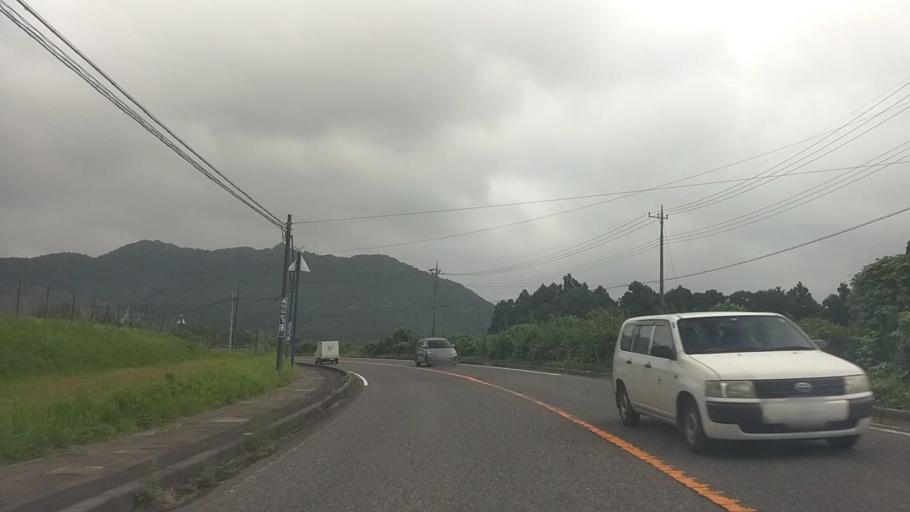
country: JP
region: Chiba
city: Kawaguchi
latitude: 35.1351
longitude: 140.0723
